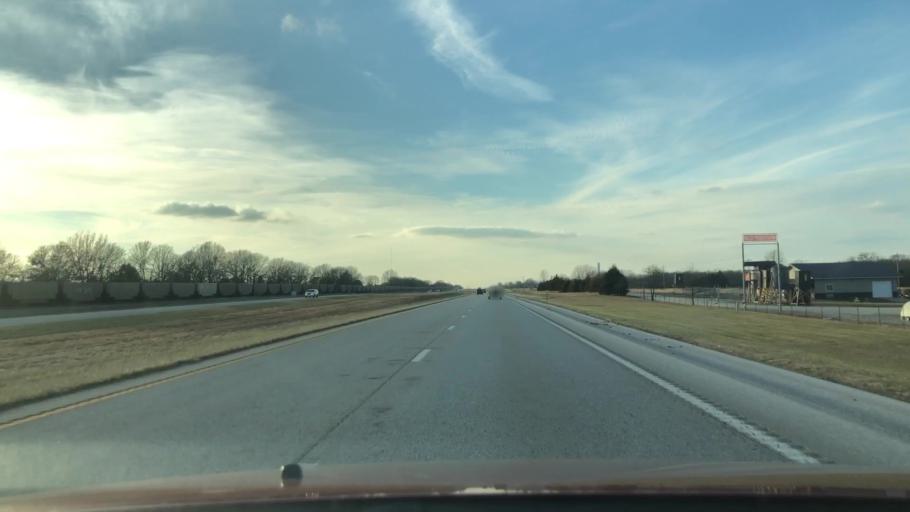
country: US
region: Missouri
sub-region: Webster County
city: Seymour
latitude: 37.1701
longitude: -92.8293
